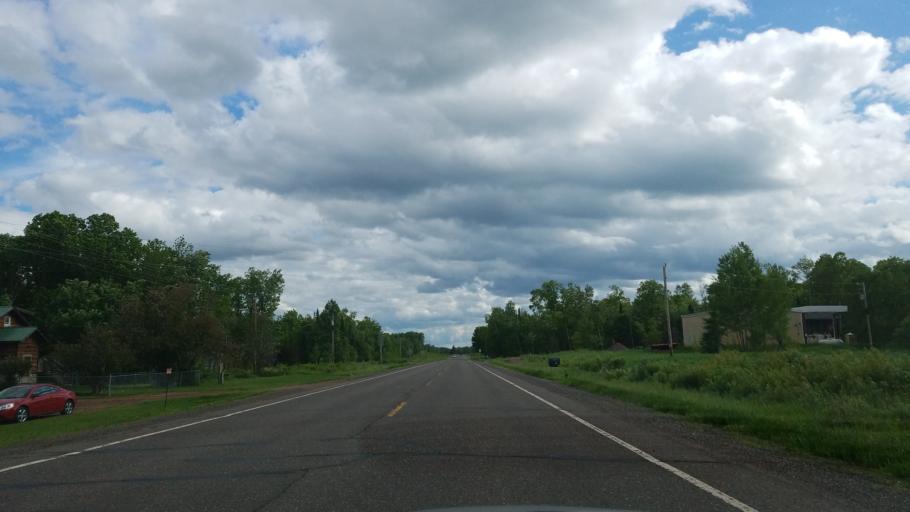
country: US
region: Wisconsin
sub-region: Washburn County
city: Spooner
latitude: 46.2151
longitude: -92.1547
